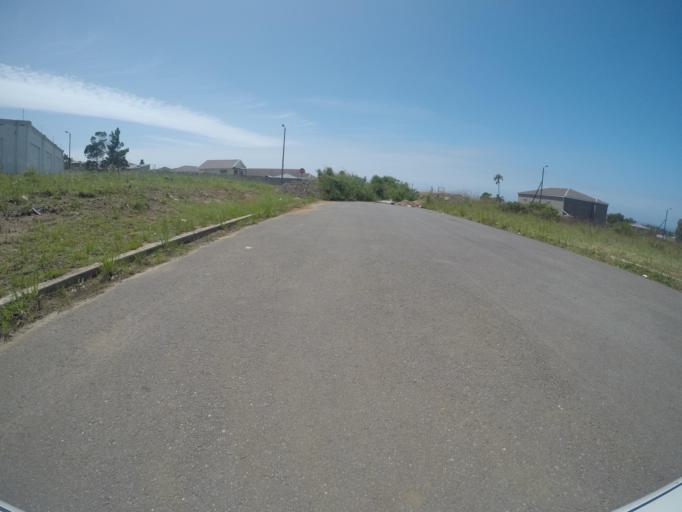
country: ZA
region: Eastern Cape
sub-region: Buffalo City Metropolitan Municipality
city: East London
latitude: -32.9427
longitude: 27.9933
